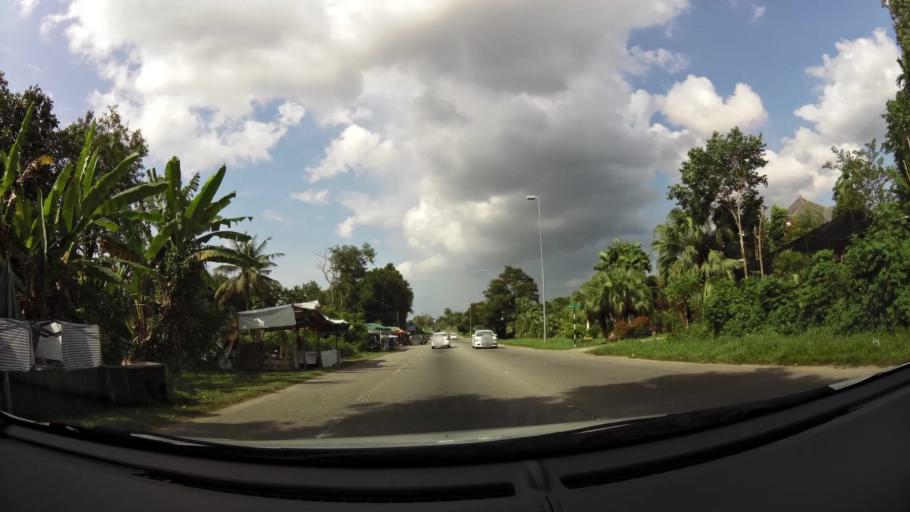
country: BN
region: Brunei and Muara
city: Bandar Seri Begawan
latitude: 4.9519
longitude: 114.9689
